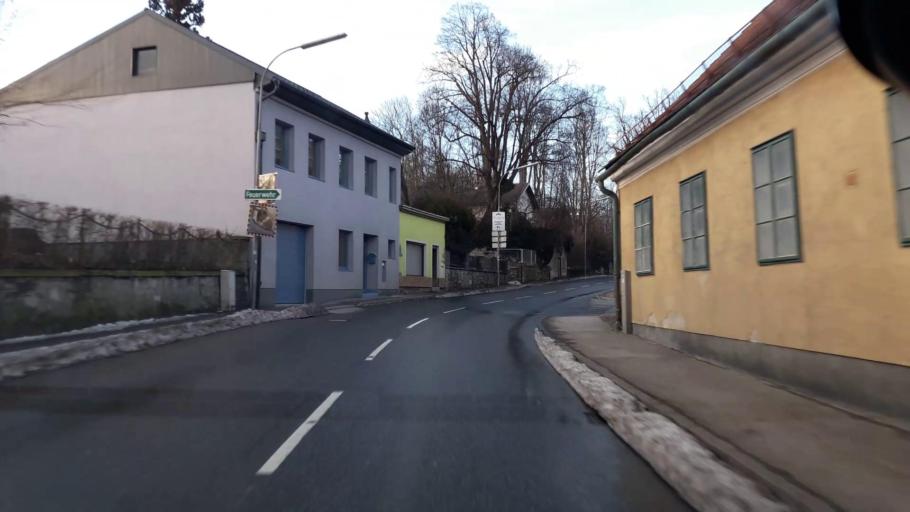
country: AT
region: Lower Austria
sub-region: Politischer Bezirk Wien-Umgebung
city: Mauerbach
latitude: 48.2467
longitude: 16.1666
